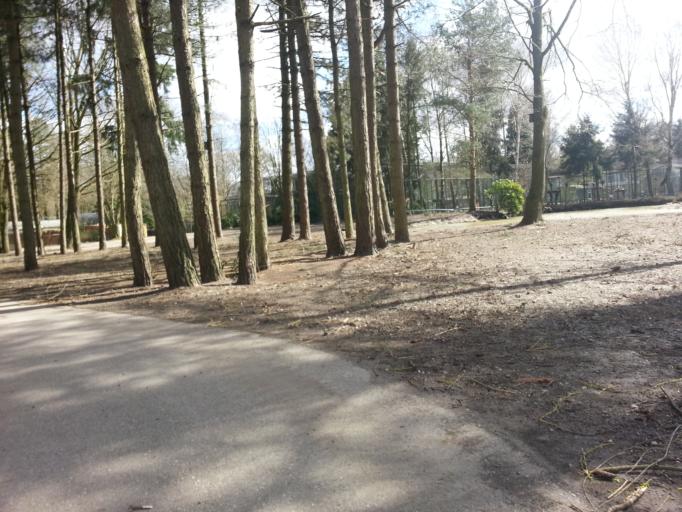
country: NL
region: North Brabant
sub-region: Gemeente Veldhoven
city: Oerle
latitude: 51.4275
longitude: 5.3506
